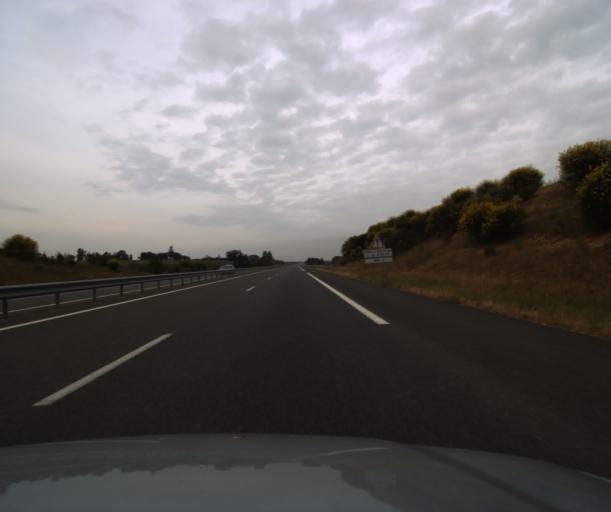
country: FR
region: Midi-Pyrenees
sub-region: Departement du Gers
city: Aubiet
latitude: 43.6544
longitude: 0.7483
